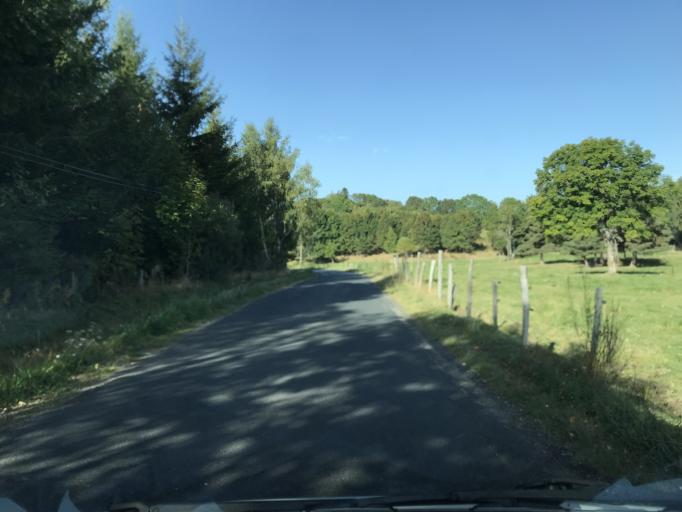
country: FR
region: Rhone-Alpes
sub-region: Departement de l'Ardeche
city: Saint-Agreve
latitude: 45.0268
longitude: 4.4317
